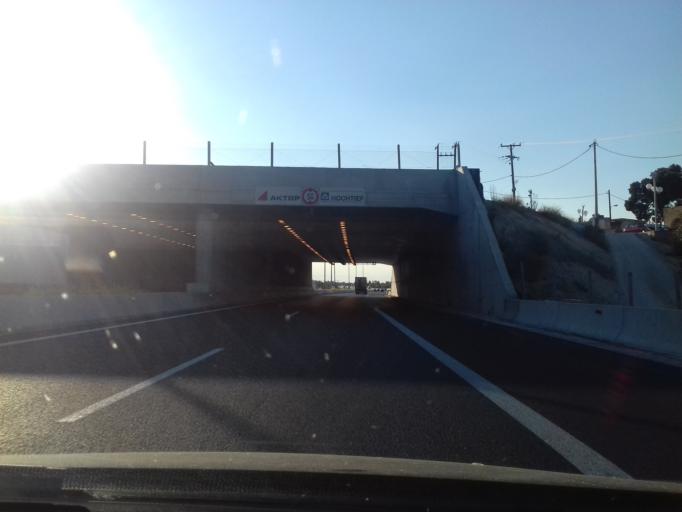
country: GR
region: Peloponnese
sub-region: Nomos Korinthias
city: Kato Dhiminio
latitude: 38.0493
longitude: 22.6854
